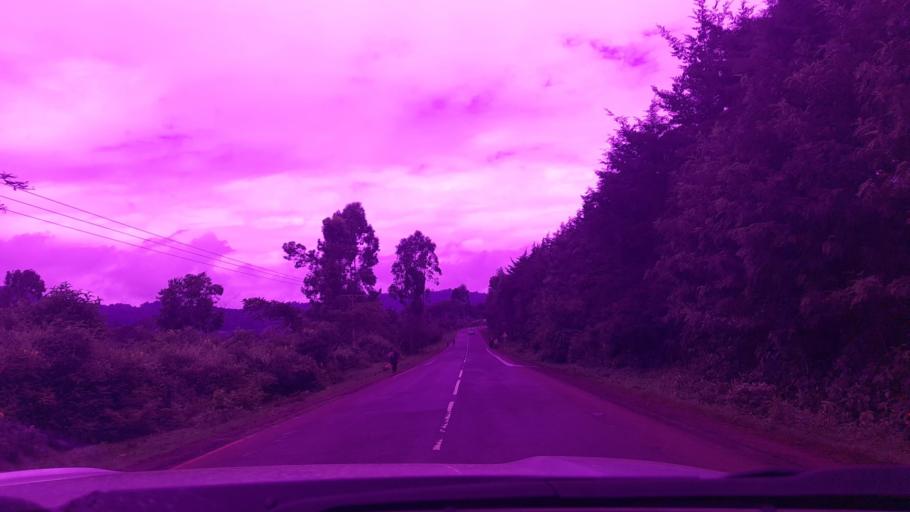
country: ET
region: Oromiya
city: Jima
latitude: 7.5549
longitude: 36.6123
